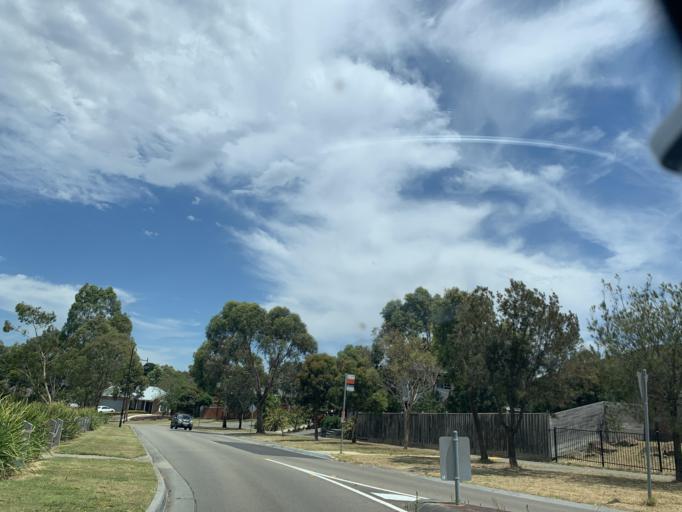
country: AU
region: Victoria
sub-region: Casey
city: Cranbourne South
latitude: -38.1455
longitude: 145.2492
